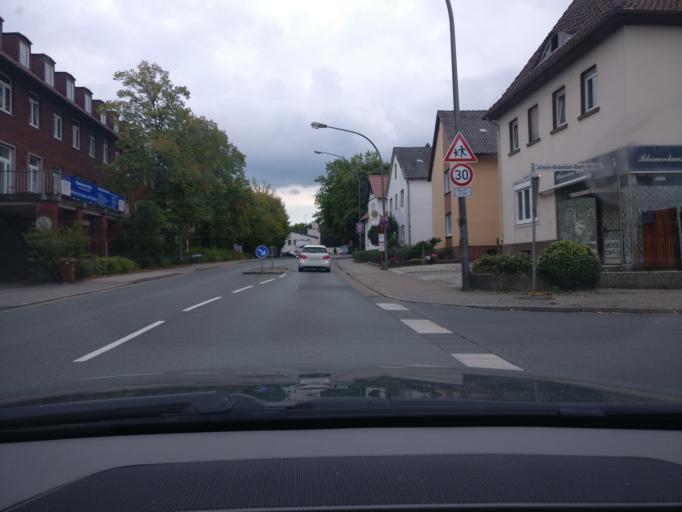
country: DE
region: Lower Saxony
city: Melle
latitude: 52.1968
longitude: 8.3417
